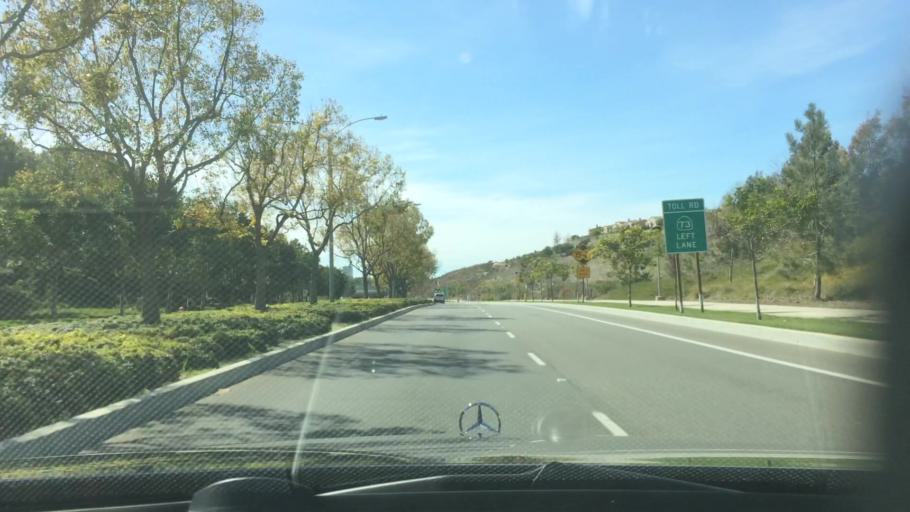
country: US
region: California
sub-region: Orange County
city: San Joaquin Hills
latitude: 33.6331
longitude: -117.8370
